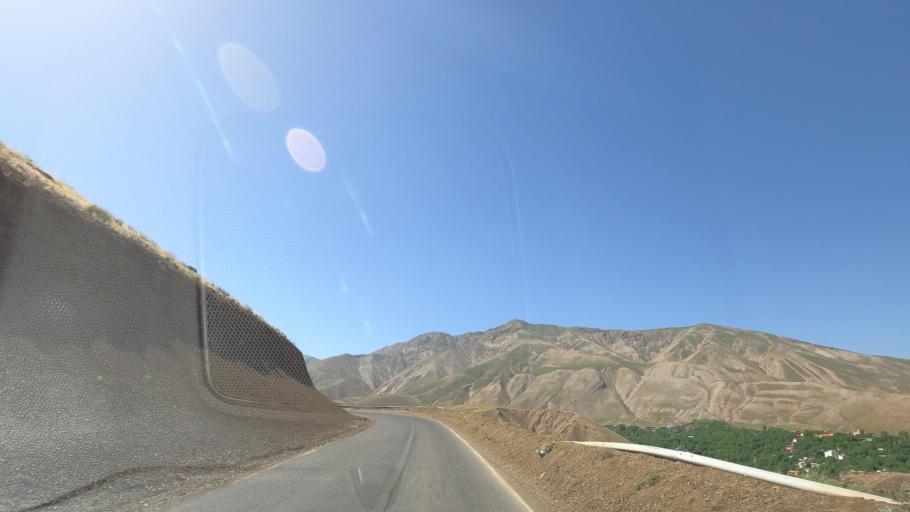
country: IR
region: Alborz
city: Karaj
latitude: 35.9336
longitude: 51.0823
